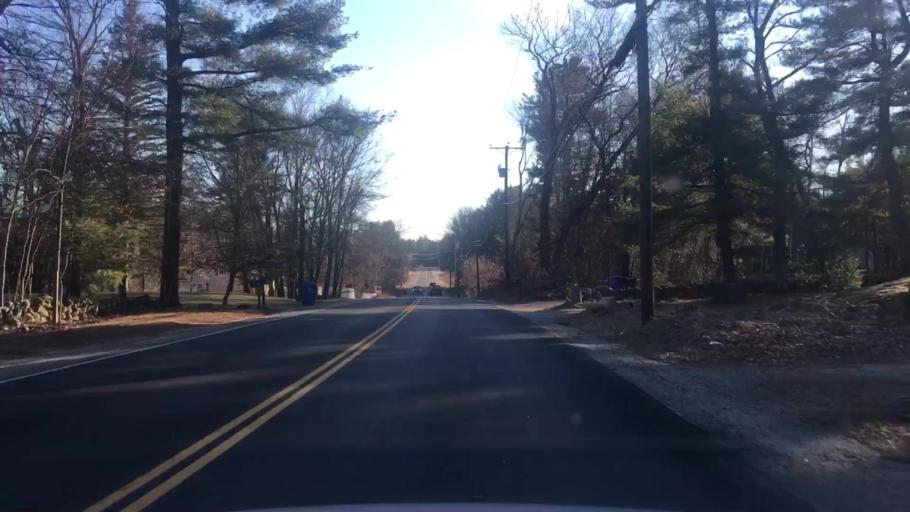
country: US
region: New Hampshire
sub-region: Rockingham County
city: Londonderry
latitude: 42.8842
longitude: -71.3820
